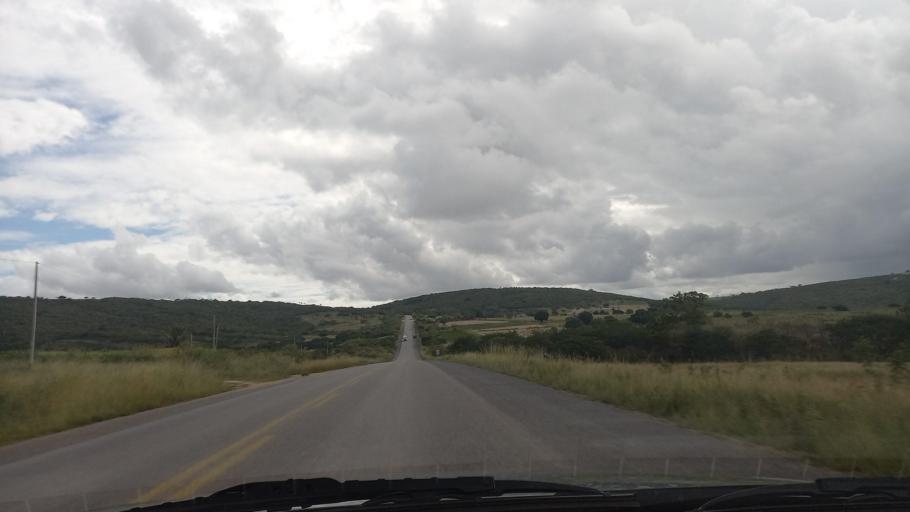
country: BR
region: Pernambuco
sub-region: Lajedo
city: Lajedo
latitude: -8.6715
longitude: -36.3883
